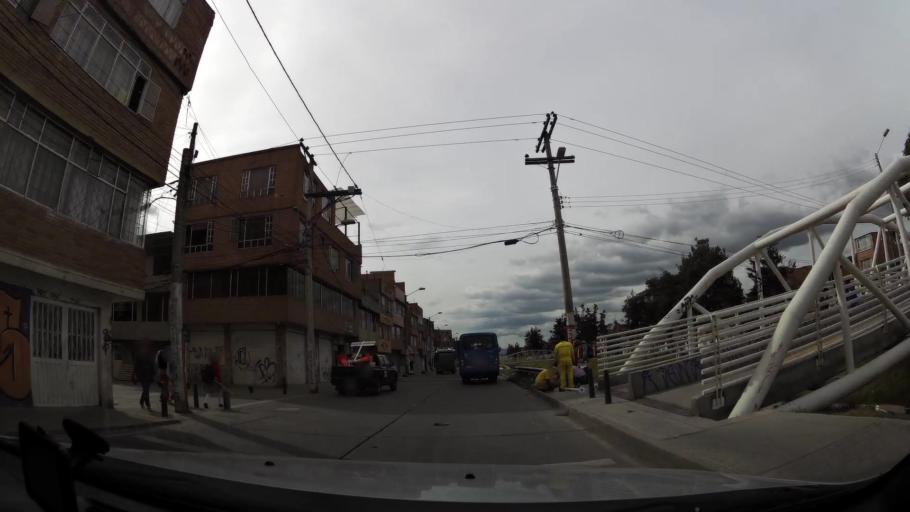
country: CO
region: Cundinamarca
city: Soacha
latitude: 4.6416
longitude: -74.1683
